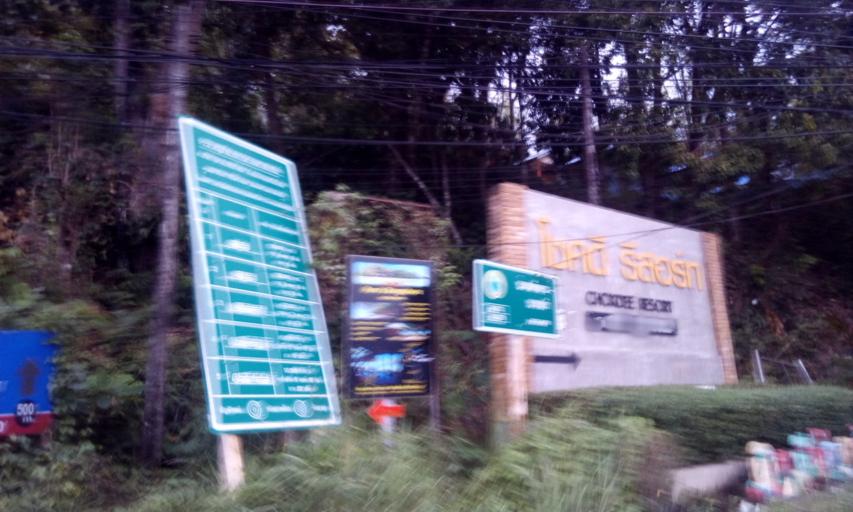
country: TH
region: Trat
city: Ko Chang Tai
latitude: 12.0382
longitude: 102.2937
